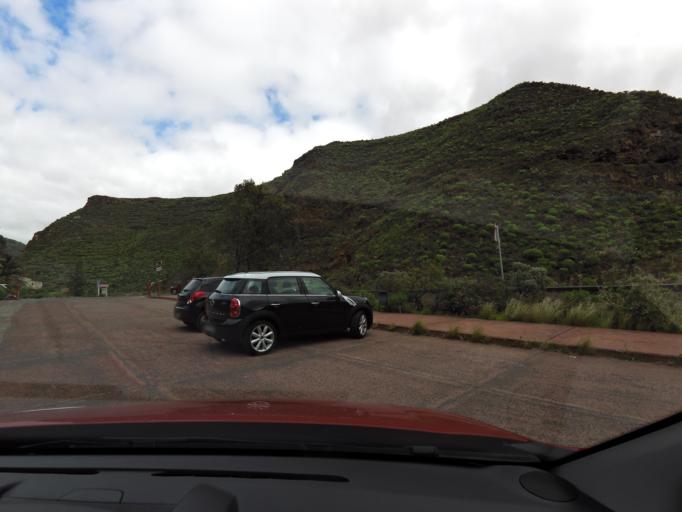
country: ES
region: Canary Islands
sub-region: Provincia de Las Palmas
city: Ingenio
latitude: 27.9240
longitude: -15.4611
